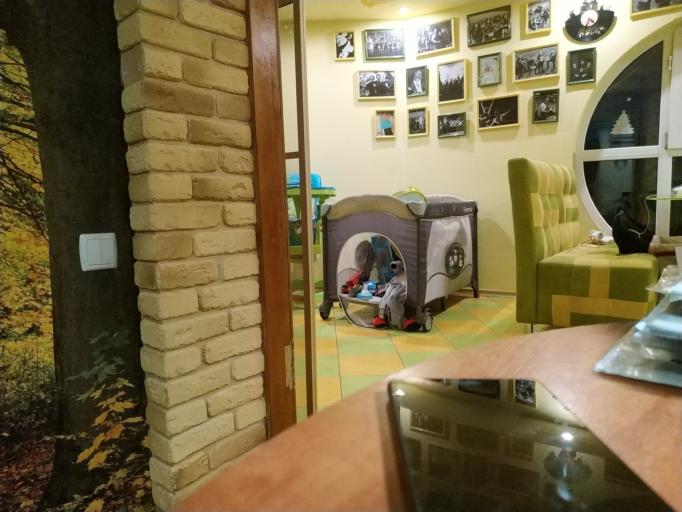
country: RU
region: Orjol
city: Znamenskoye
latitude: 53.1247
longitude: 35.6499
